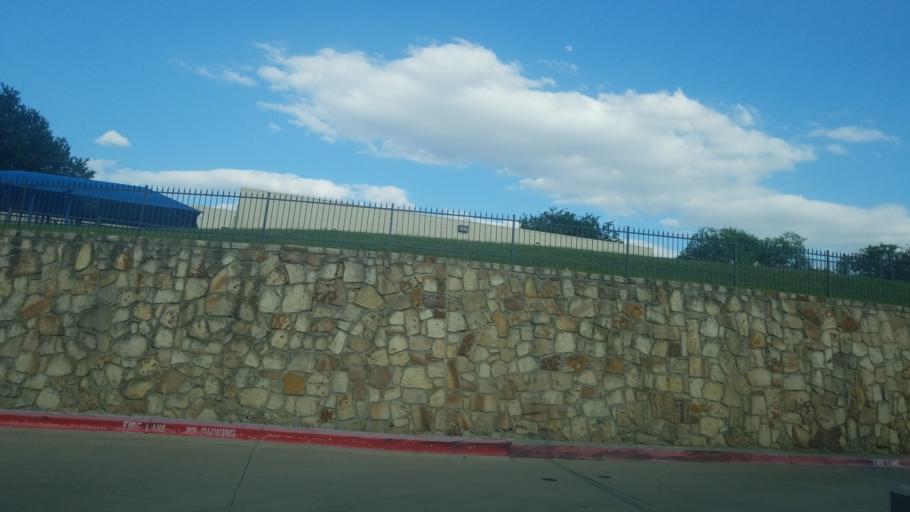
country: US
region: Texas
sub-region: Dallas County
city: Irving
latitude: 32.8862
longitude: -96.9632
